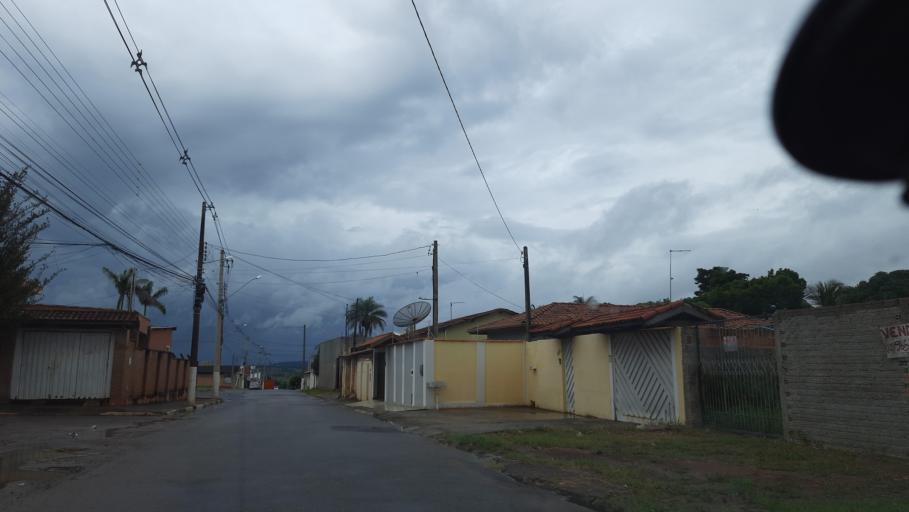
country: BR
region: Sao Paulo
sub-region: Casa Branca
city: Casa Branca
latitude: -21.7772
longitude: -47.0971
